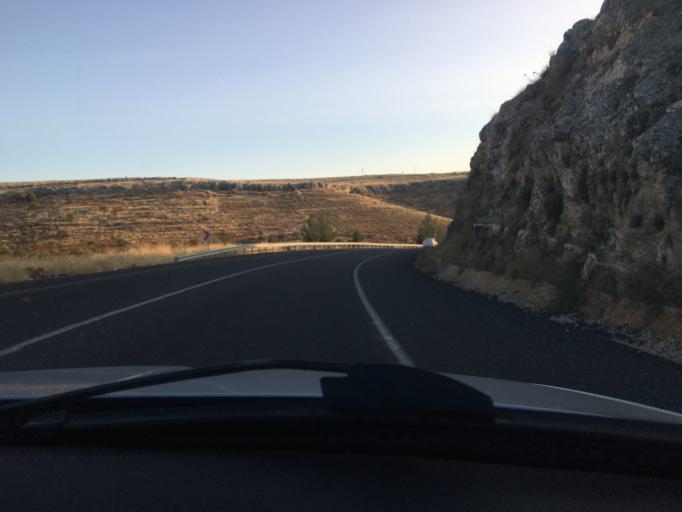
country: TR
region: Sanliurfa
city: Halfeti
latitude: 37.2249
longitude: 37.9596
